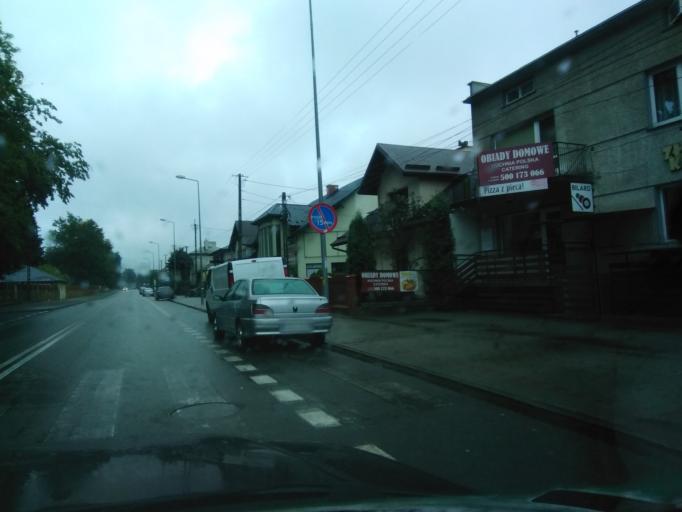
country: PL
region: Subcarpathian Voivodeship
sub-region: Powiat debicki
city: Debica
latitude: 50.0608
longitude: 21.4063
